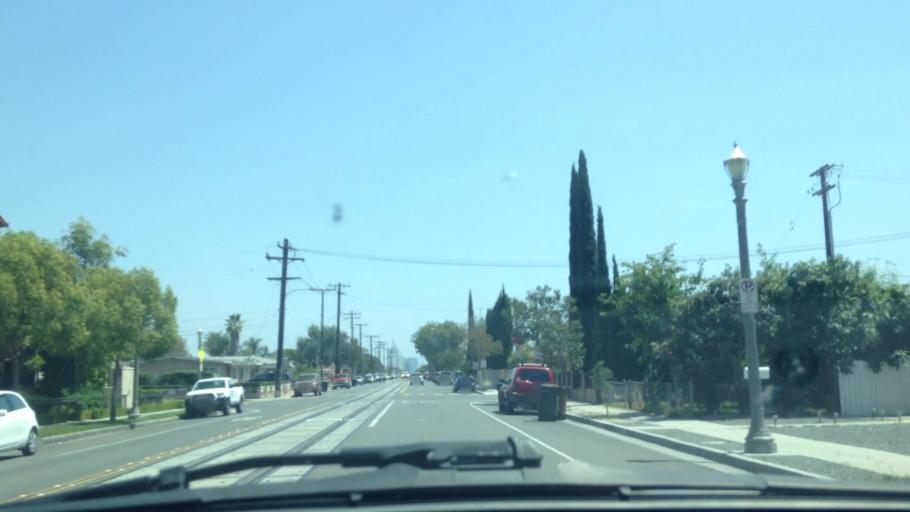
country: US
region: California
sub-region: Orange County
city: Anaheim
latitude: 33.8282
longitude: -117.9075
